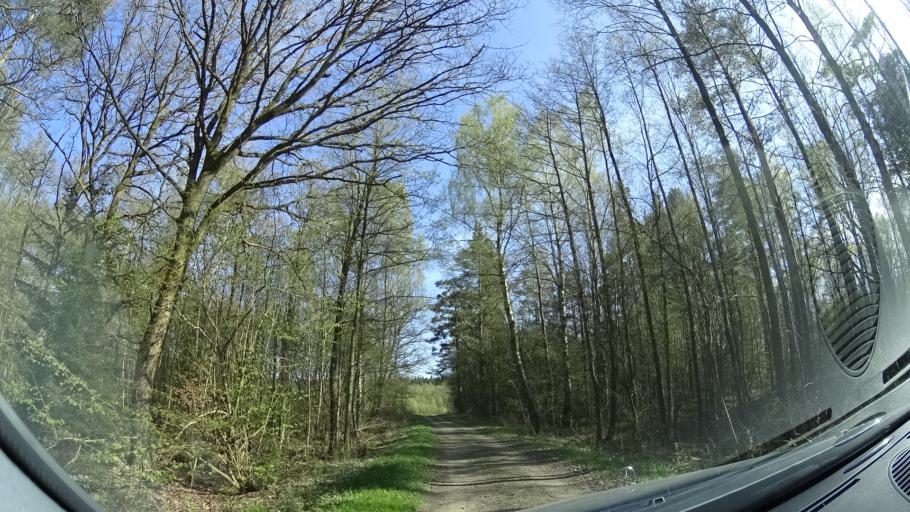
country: SE
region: Skane
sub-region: Hassleholms Kommun
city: Tormestorp
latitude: 56.1004
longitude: 13.6706
